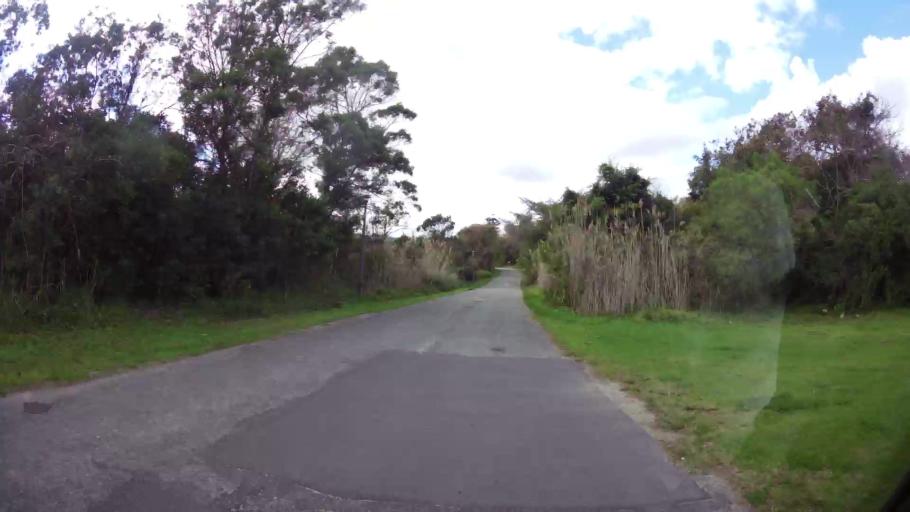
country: ZA
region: Western Cape
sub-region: Eden District Municipality
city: Knysna
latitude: -34.0589
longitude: 23.0811
